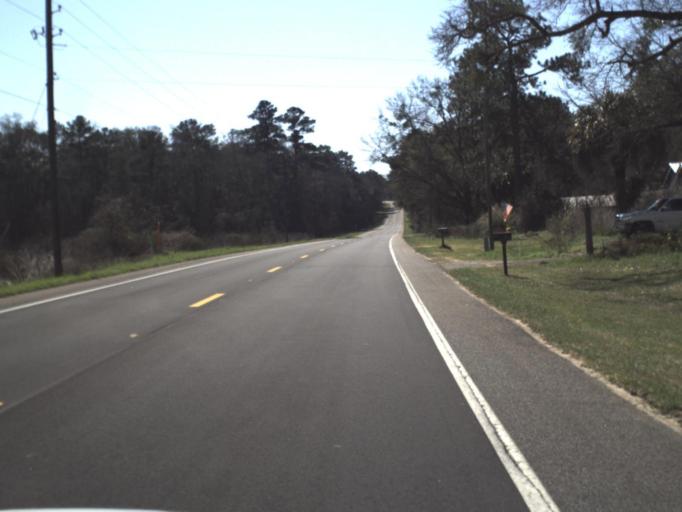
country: US
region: Florida
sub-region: Jackson County
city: Marianna
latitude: 30.6170
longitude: -85.1493
